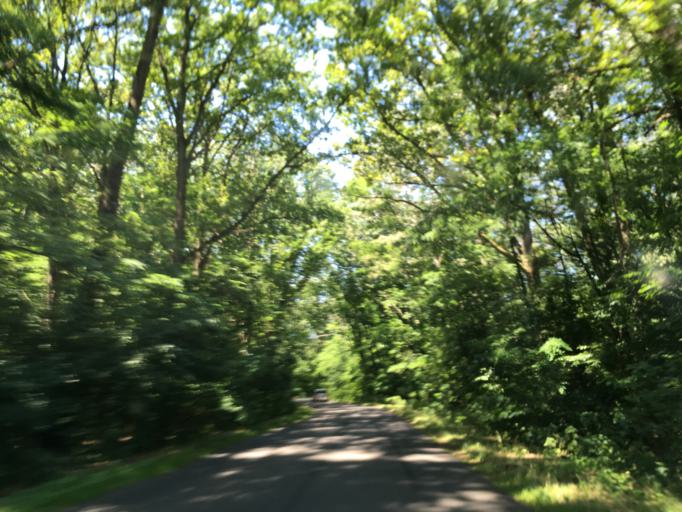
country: HU
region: Hajdu-Bihar
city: Mikepercs
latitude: 47.4689
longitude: 21.6906
